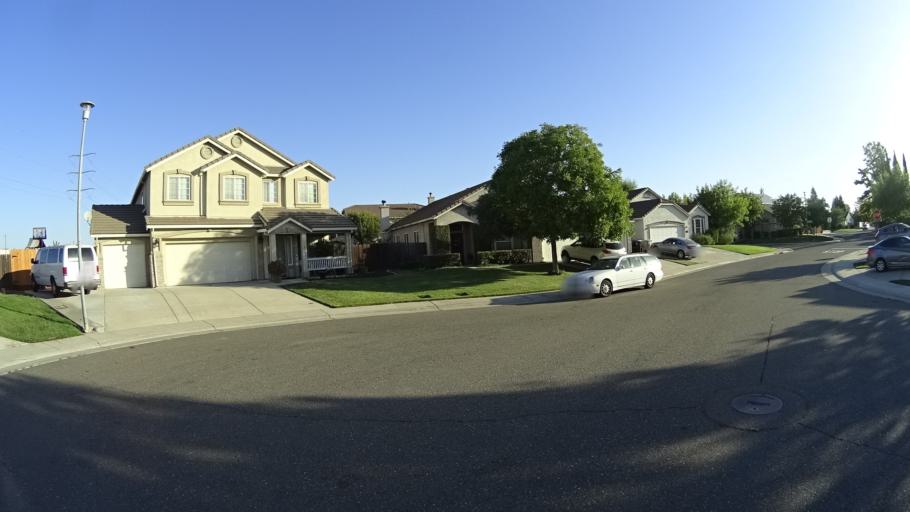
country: US
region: California
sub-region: Sacramento County
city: Laguna
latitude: 38.4259
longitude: -121.4556
